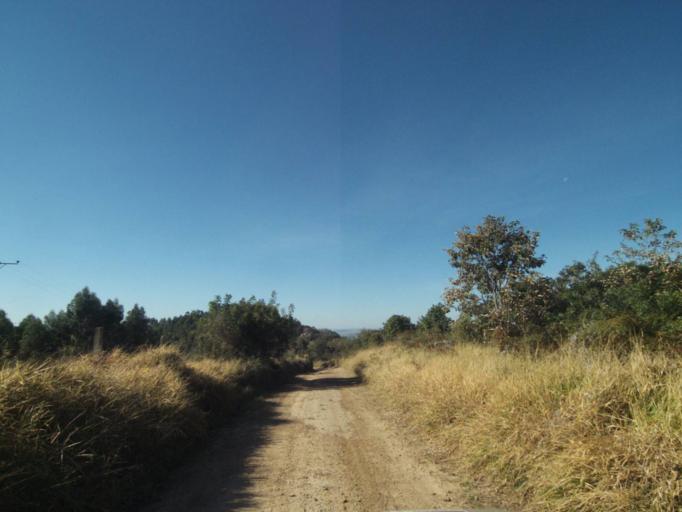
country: BR
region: Parana
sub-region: Tibagi
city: Tibagi
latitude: -24.5763
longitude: -50.4784
